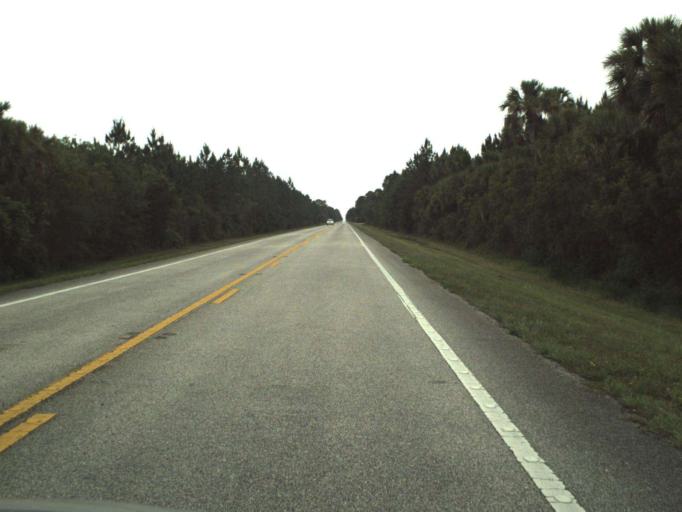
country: US
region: Florida
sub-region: Brevard County
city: Mims
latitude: 28.6693
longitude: -80.9687
